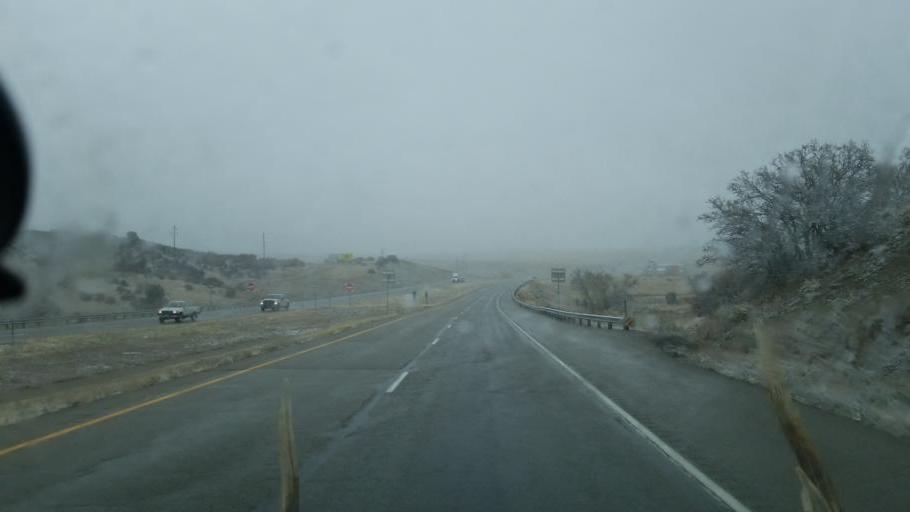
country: US
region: Colorado
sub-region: Pueblo County
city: Colorado City
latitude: 37.9069
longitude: -104.8289
